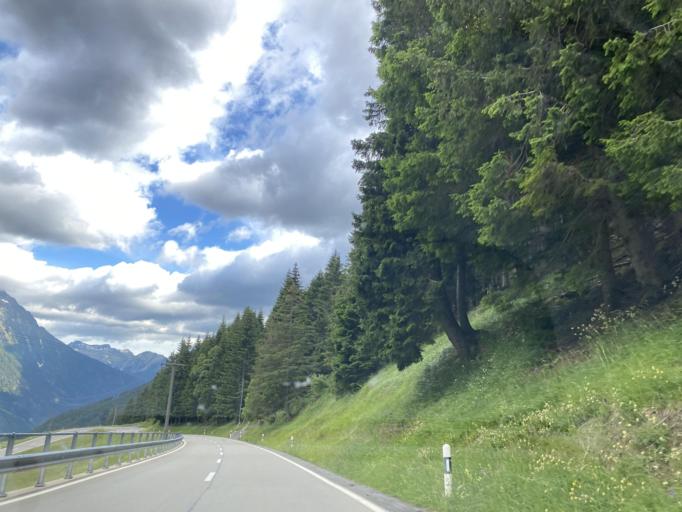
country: CH
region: Grisons
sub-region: Moesa District
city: Mesocco
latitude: 46.4366
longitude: 9.2039
